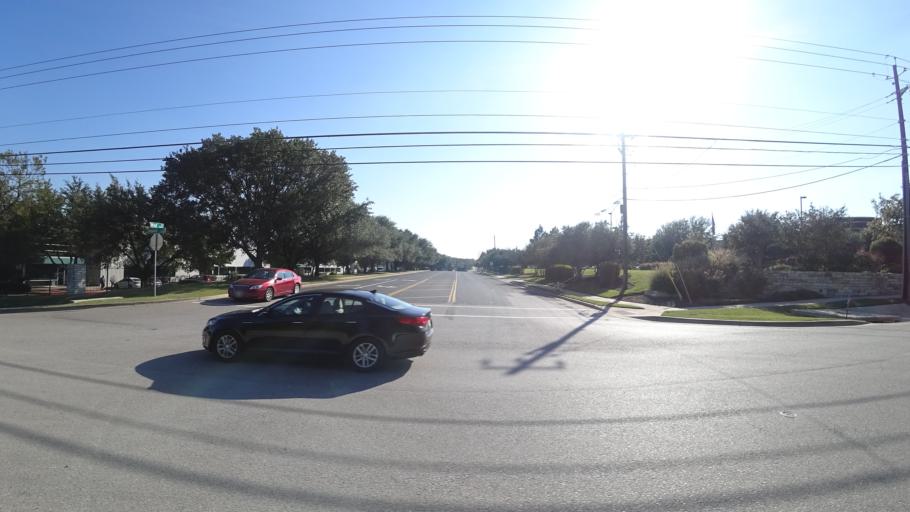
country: US
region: Texas
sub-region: Travis County
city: Wells Branch
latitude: 30.3445
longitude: -97.6684
